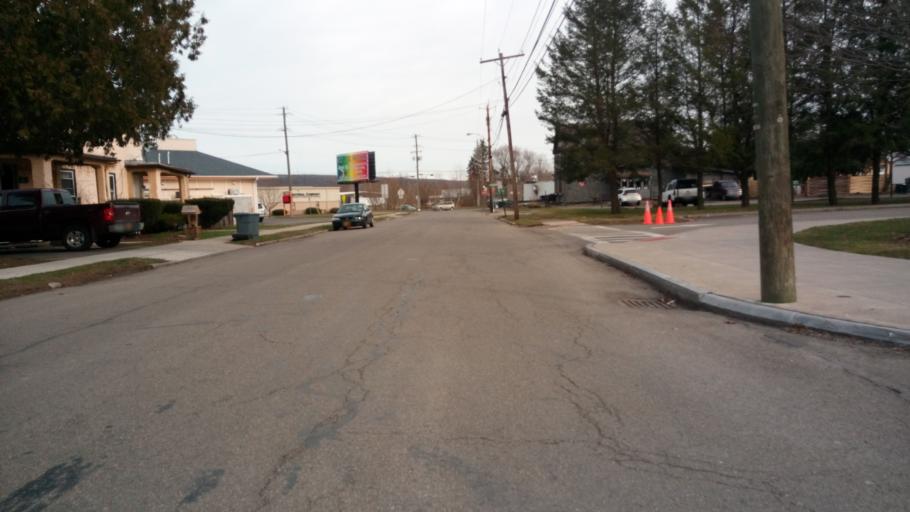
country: US
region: New York
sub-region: Chemung County
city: Elmira Heights
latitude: 42.1125
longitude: -76.8221
